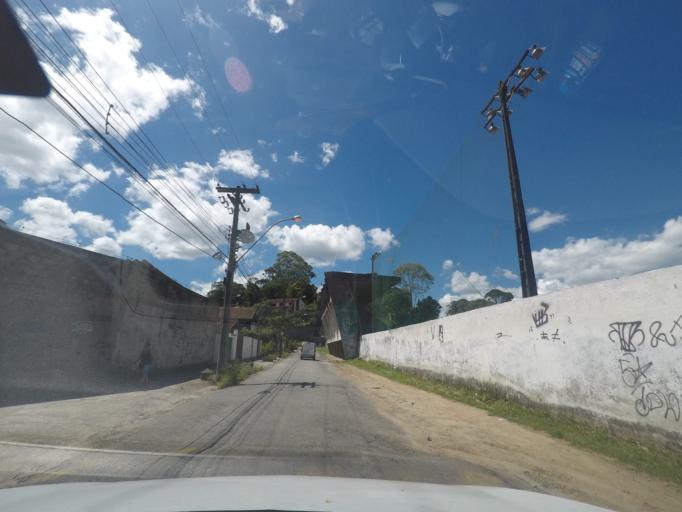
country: BR
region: Rio de Janeiro
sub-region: Teresopolis
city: Teresopolis
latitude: -22.4305
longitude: -42.9781
